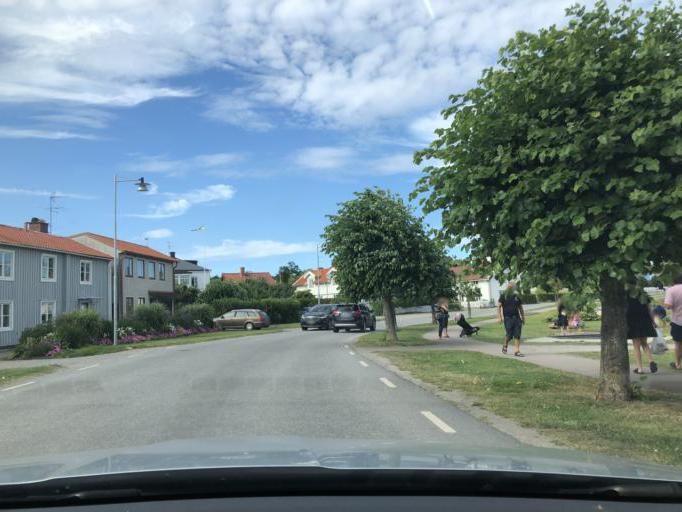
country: SE
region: Soedermanland
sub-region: Strangnas Kommun
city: Mariefred
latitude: 59.2594
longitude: 17.2250
